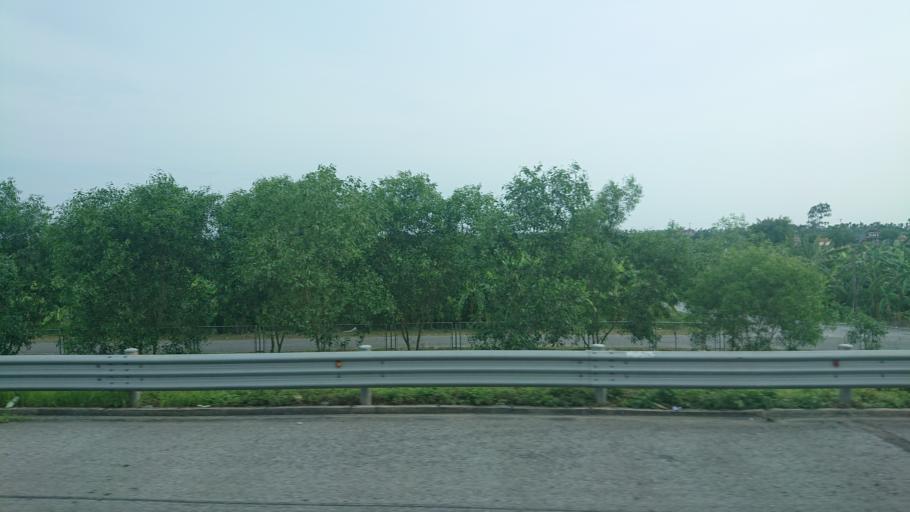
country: VN
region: Hai Duong
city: Tu Ky
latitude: 20.8293
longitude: 106.4524
